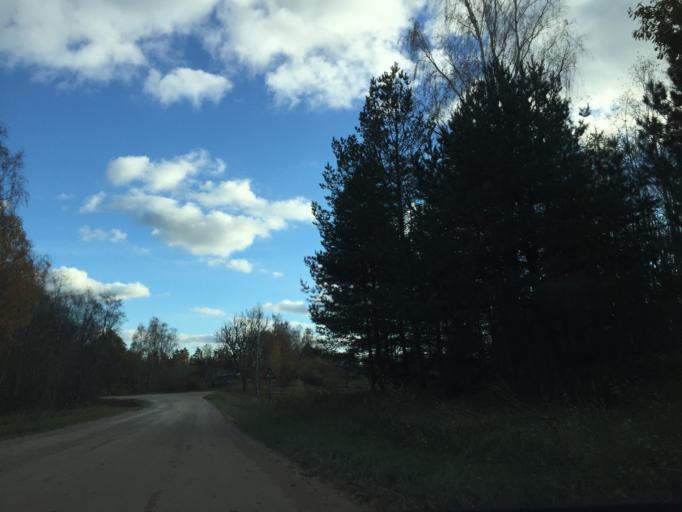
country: LV
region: Tukuma Rajons
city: Tukums
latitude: 56.9615
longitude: 22.9780
